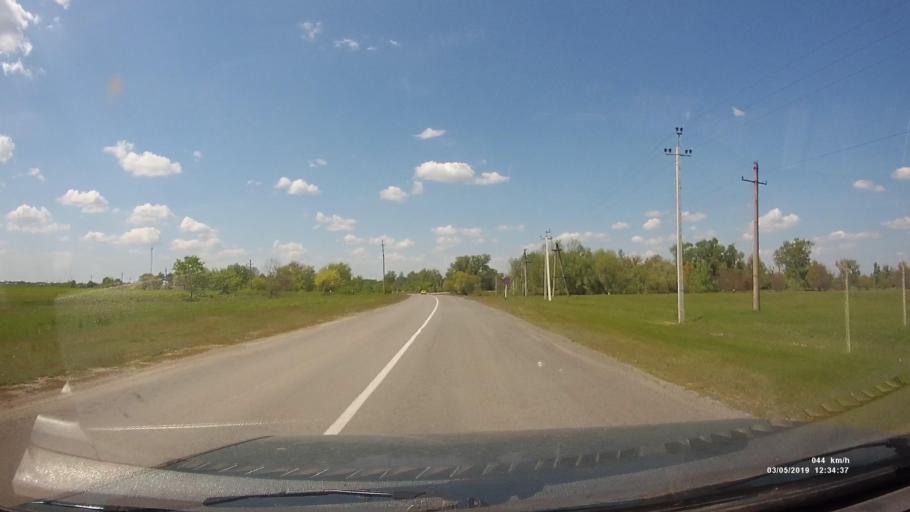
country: RU
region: Rostov
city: Semikarakorsk
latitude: 47.5222
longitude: 40.7685
